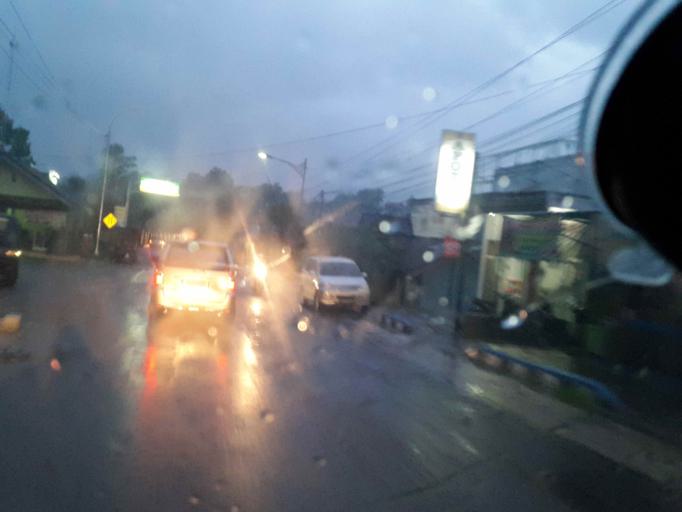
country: ID
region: Central Java
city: Wonosobo
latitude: -7.3883
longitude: 109.6915
